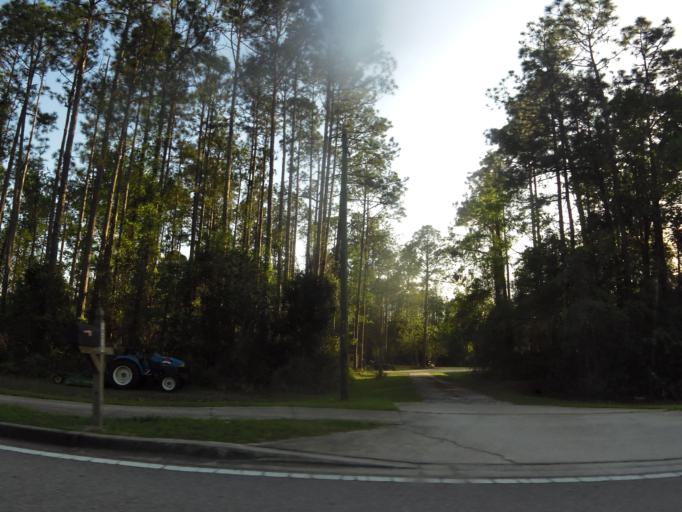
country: US
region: Florida
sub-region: Saint Johns County
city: Fruit Cove
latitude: 30.0683
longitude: -81.5075
